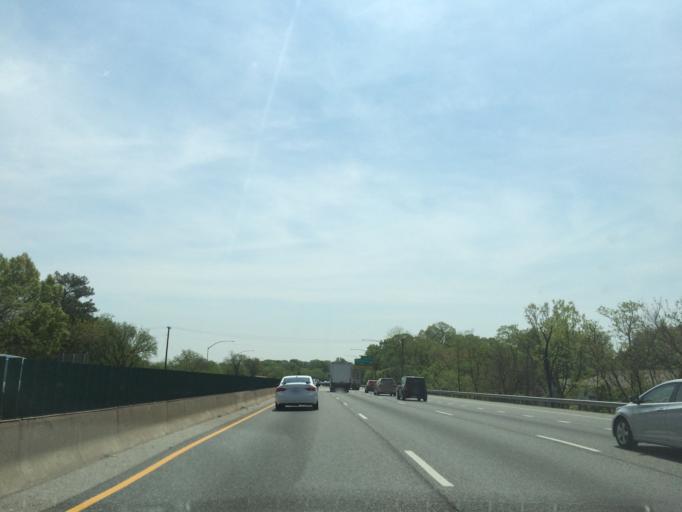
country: US
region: Maryland
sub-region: Baltimore County
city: Catonsville
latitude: 39.2827
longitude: -76.7326
